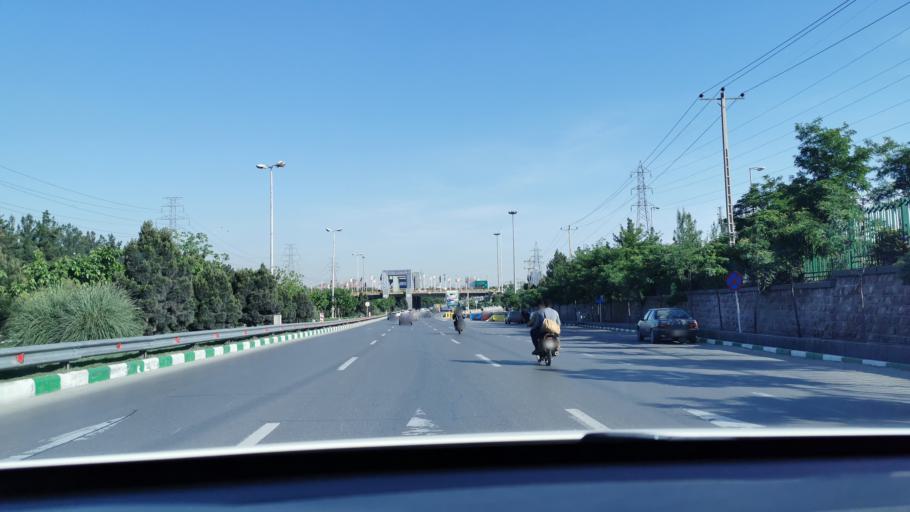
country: IR
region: Razavi Khorasan
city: Mashhad
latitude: 36.2610
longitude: 59.5853
